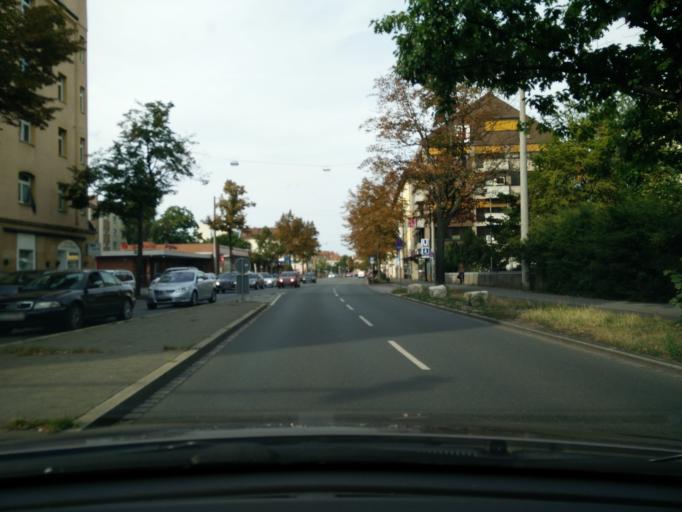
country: DE
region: Bavaria
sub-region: Regierungsbezirk Mittelfranken
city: Grossreuth bei Schweinau
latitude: 49.4277
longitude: 11.0430
